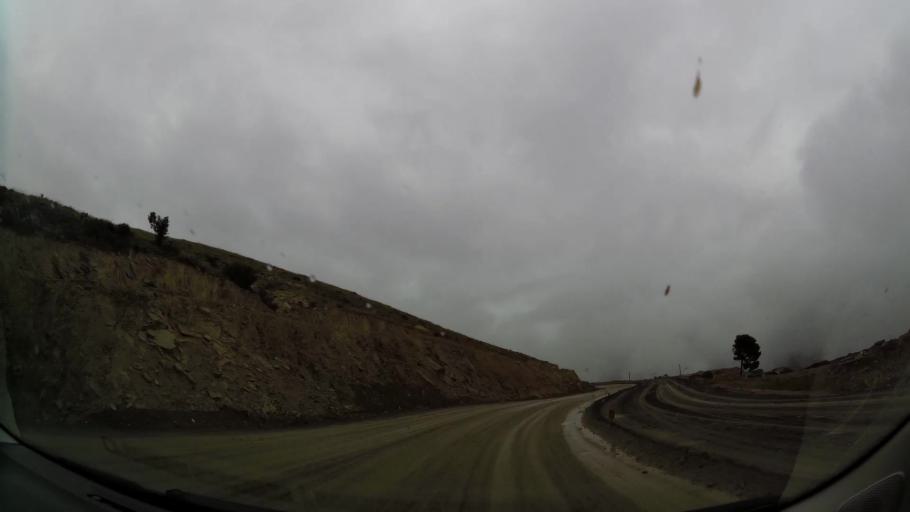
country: MA
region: Taza-Al Hoceima-Taounate
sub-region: Taza
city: Ajdir
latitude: 34.9017
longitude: -3.7862
